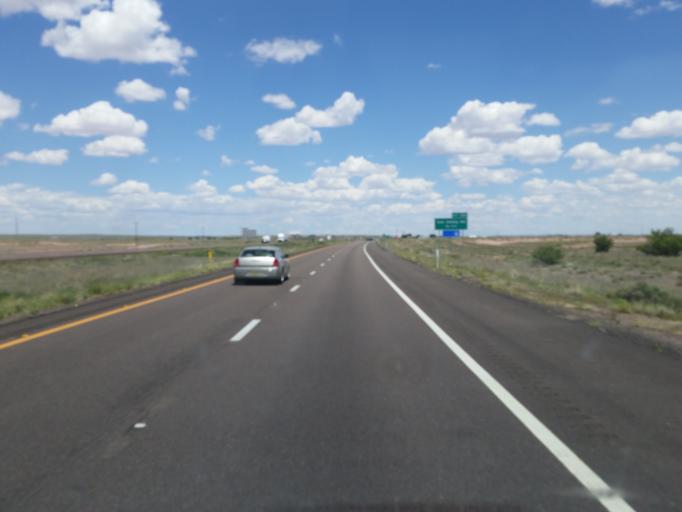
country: US
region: Arizona
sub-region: Navajo County
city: Holbrook
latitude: 34.9768
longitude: -110.0754
